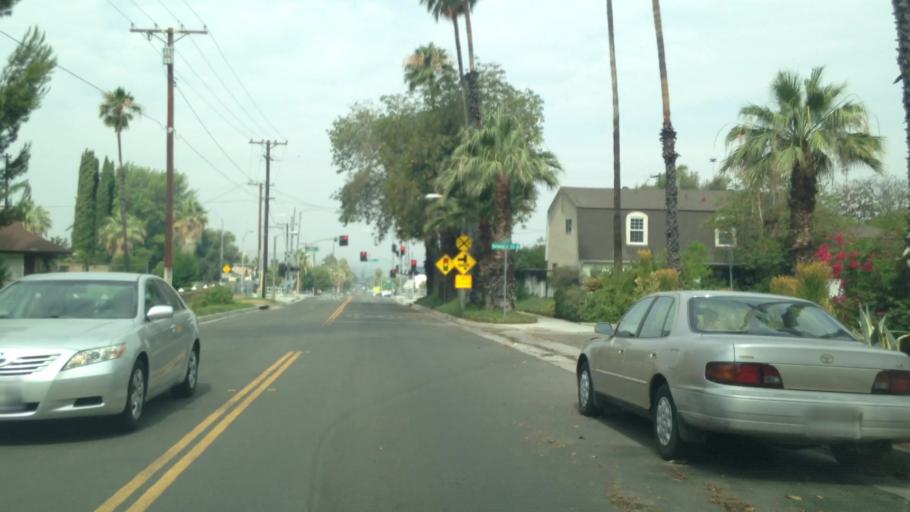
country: US
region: California
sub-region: Riverside County
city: Highgrove
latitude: 33.9902
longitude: -117.3311
